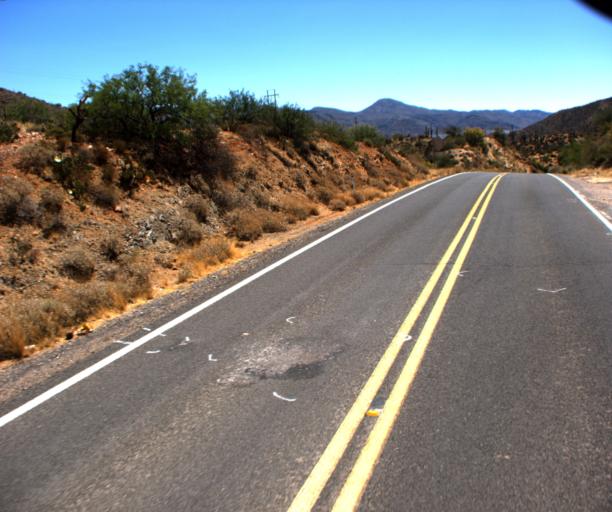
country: US
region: Arizona
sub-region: Pinal County
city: Superior
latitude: 33.1794
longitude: -111.0396
